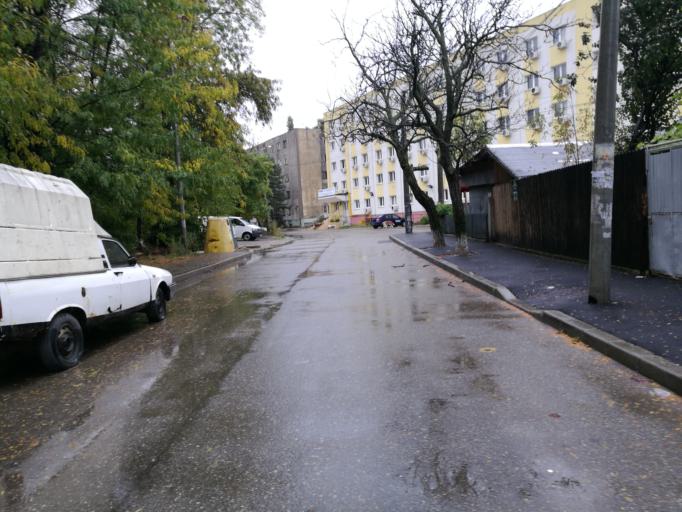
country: RO
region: Ilfov
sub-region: Comuna Chiajna
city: Rosu
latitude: 44.4496
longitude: 26.0505
